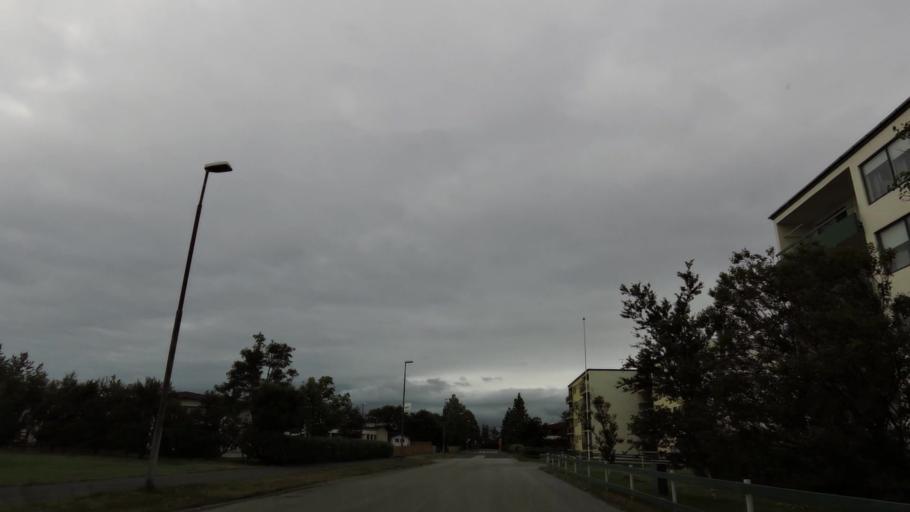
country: IS
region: Capital Region
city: Hafnarfjoerdur
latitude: 64.0805
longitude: -21.9615
